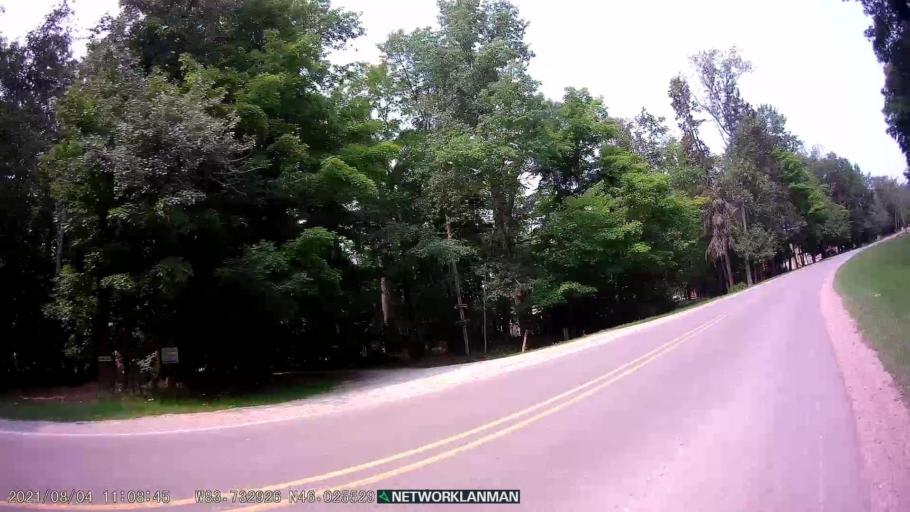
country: CA
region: Ontario
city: Thessalon
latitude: 46.0265
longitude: -83.7323
